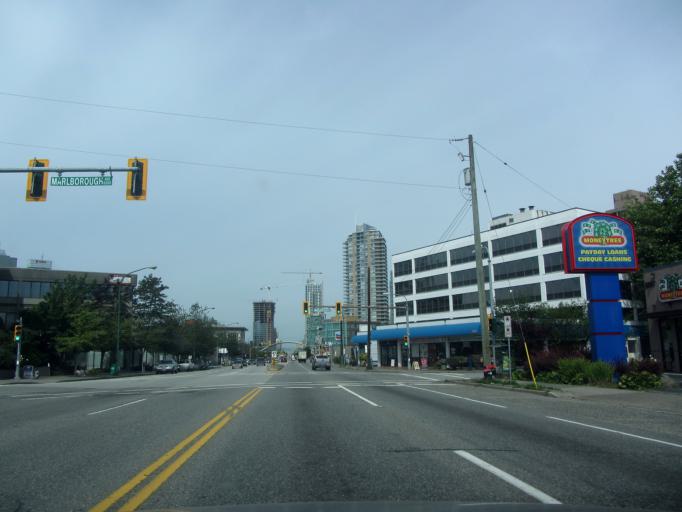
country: CA
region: British Columbia
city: Burnaby
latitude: 49.2201
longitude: -122.9729
